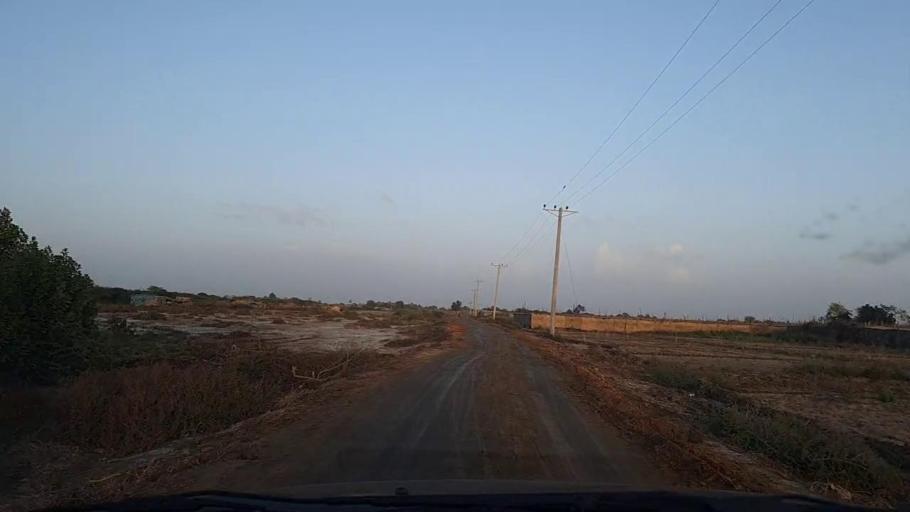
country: PK
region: Sindh
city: Keti Bandar
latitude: 24.1627
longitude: 67.6115
